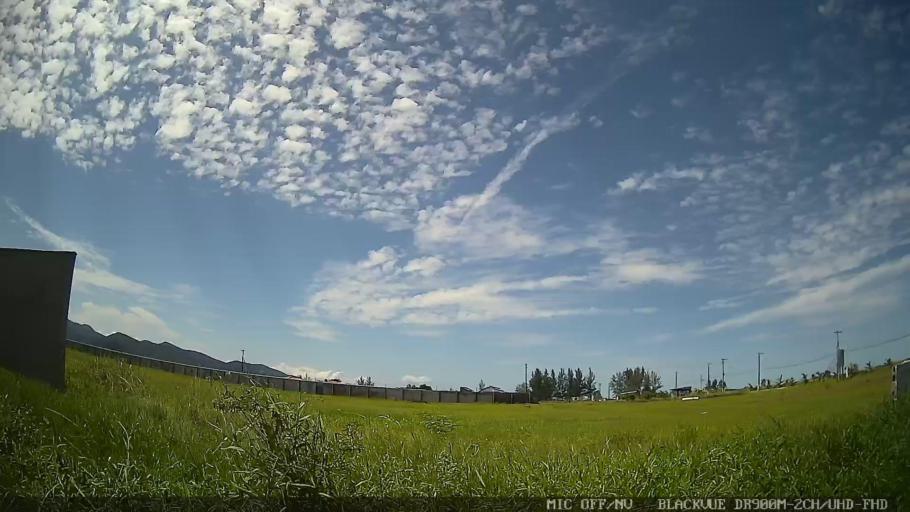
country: BR
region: Sao Paulo
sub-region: Iguape
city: Iguape
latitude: -24.7283
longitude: -47.5159
